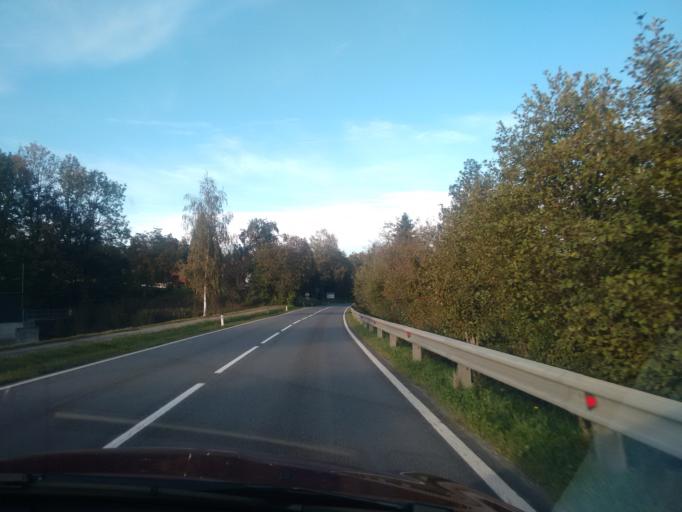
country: AT
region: Upper Austria
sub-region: Politischer Bezirk Vocklabruck
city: Niederthalheim
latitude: 48.1662
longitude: 13.7504
